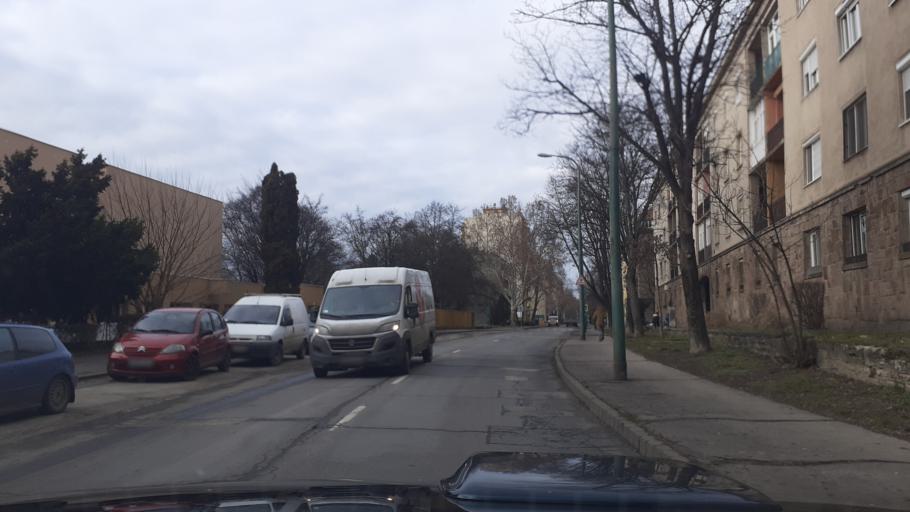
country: HU
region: Fejer
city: dunaujvaros
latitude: 46.9615
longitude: 18.9294
